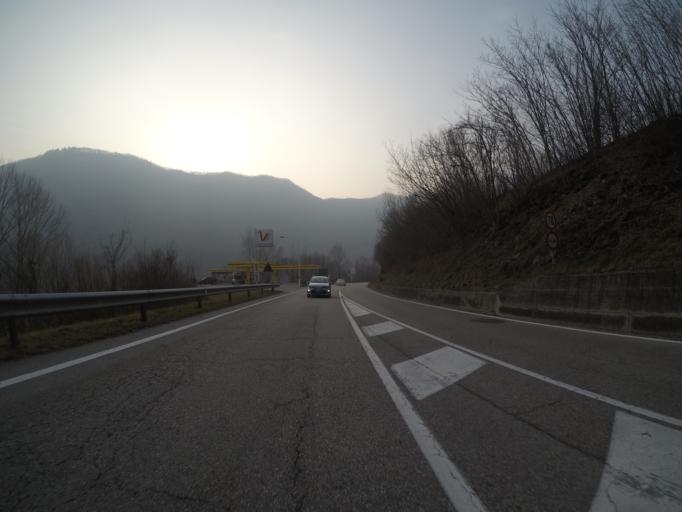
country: IT
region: Veneto
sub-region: Provincia di Belluno
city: Vas
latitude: 45.9363
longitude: 11.9317
